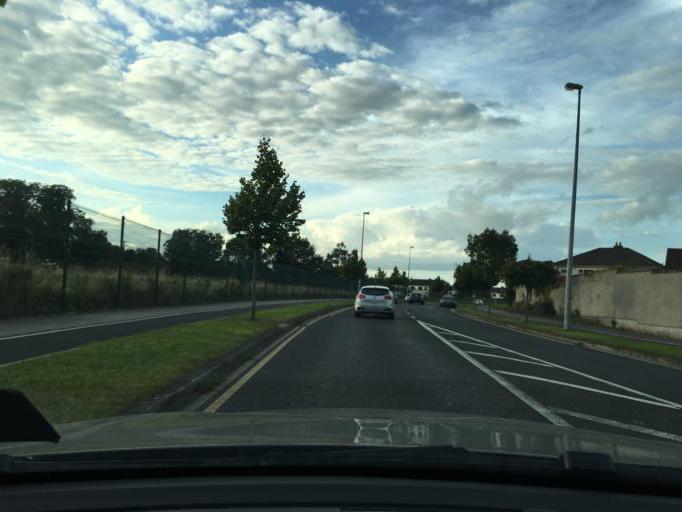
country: IE
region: Leinster
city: Hartstown
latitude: 53.3844
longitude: -6.4192
